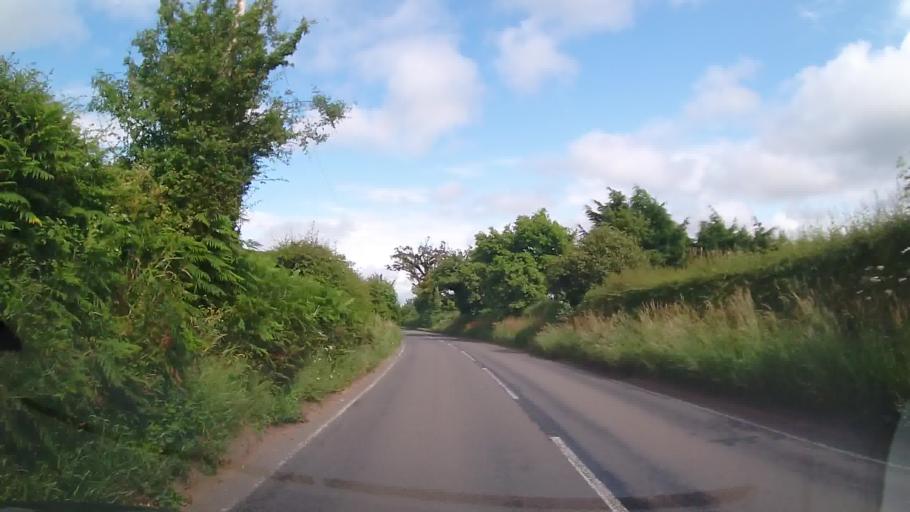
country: GB
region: England
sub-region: Shropshire
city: Great Ness
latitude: 52.7958
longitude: -2.9190
